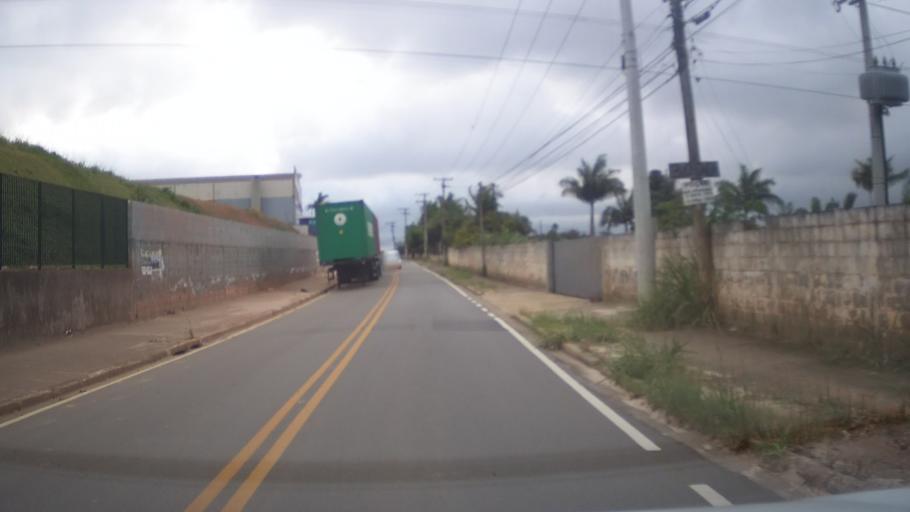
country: BR
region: Sao Paulo
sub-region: Aruja
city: Aruja
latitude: -23.4037
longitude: -46.3559
